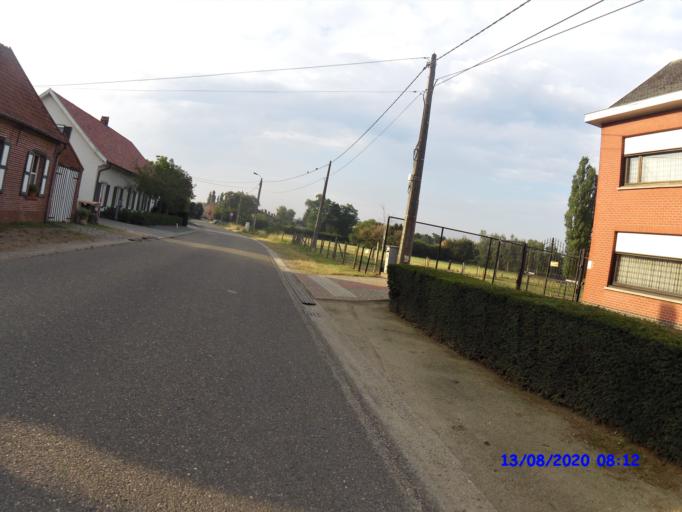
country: BE
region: Flanders
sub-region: Provincie Antwerpen
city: Brecht
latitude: 51.3524
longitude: 4.6653
